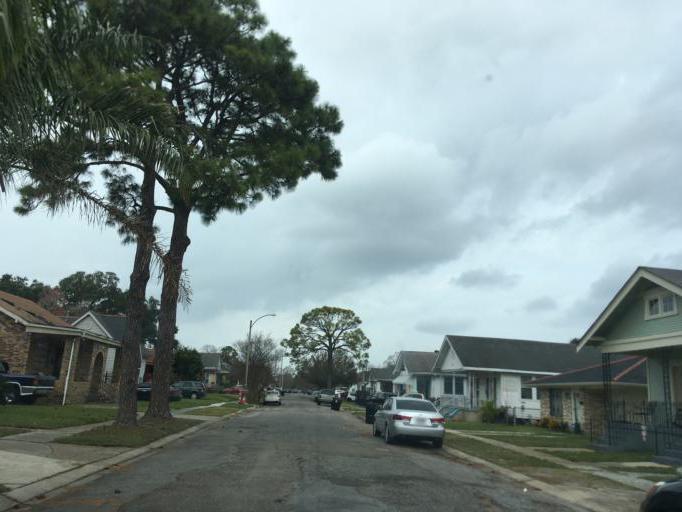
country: US
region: Louisiana
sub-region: Orleans Parish
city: New Orleans
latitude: 29.9936
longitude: -90.0532
